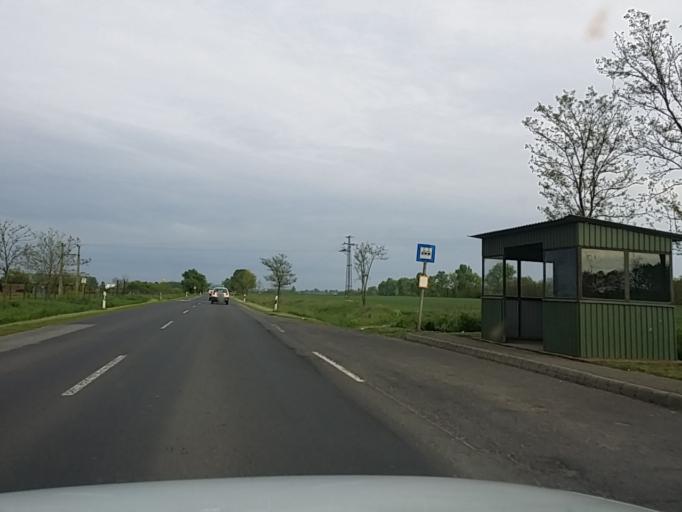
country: HU
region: Jasz-Nagykun-Szolnok
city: Jaszbereny
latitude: 47.5255
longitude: 19.8574
